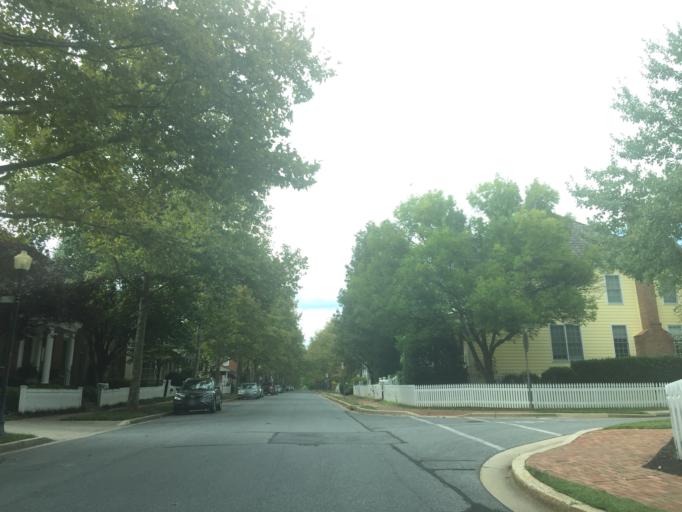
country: US
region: Maryland
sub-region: Montgomery County
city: North Potomac
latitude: 39.1144
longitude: -77.2424
